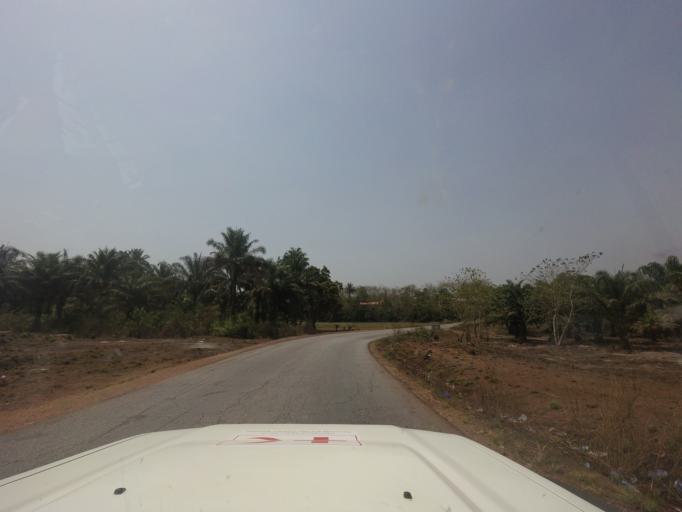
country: GN
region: Kindia
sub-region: Kindia
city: Kindia
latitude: 9.9647
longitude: -12.9368
